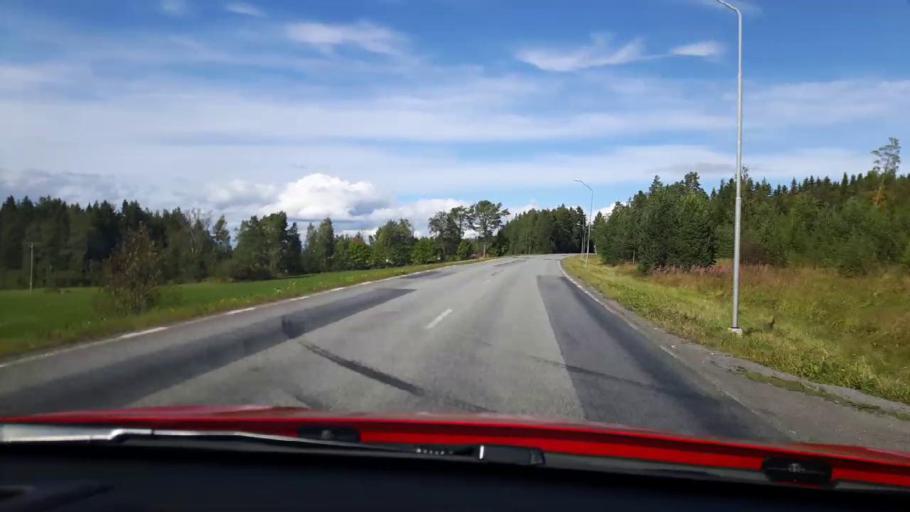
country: SE
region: Jaemtland
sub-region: OEstersunds Kommun
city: Ostersund
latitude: 63.0893
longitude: 14.4362
